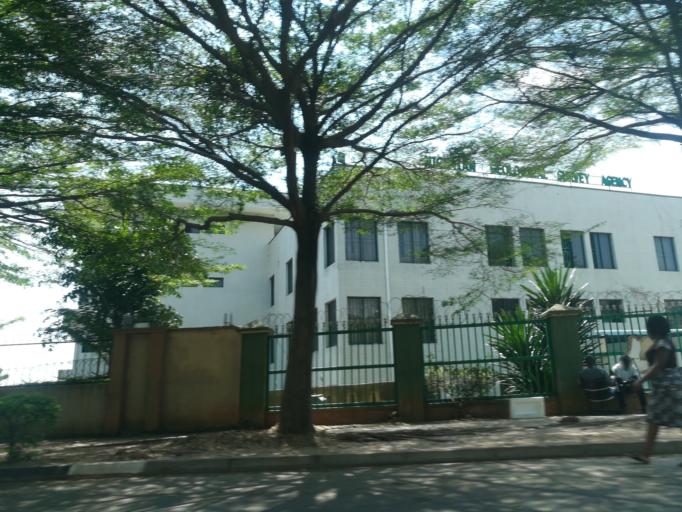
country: NG
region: Abuja Federal Capital Territory
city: Abuja
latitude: 9.0608
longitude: 7.4514
